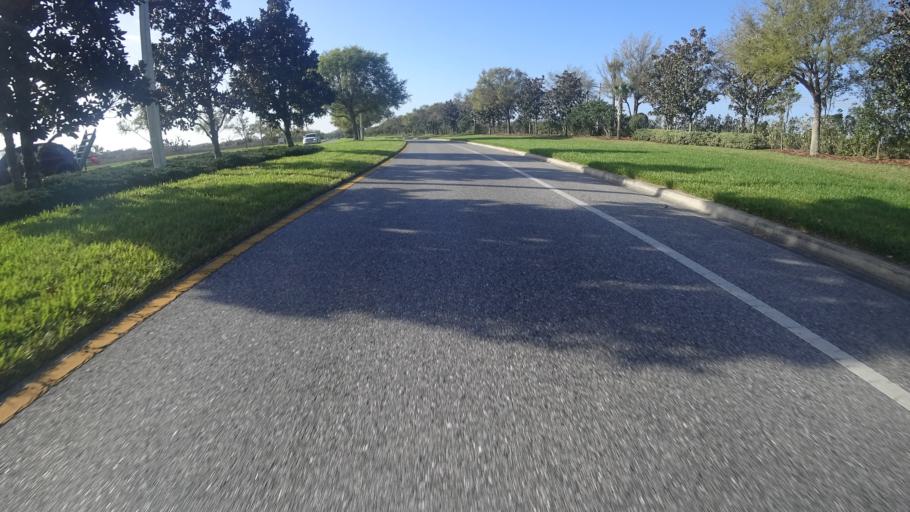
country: US
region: Florida
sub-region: Manatee County
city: Ellenton
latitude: 27.5635
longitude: -82.4580
